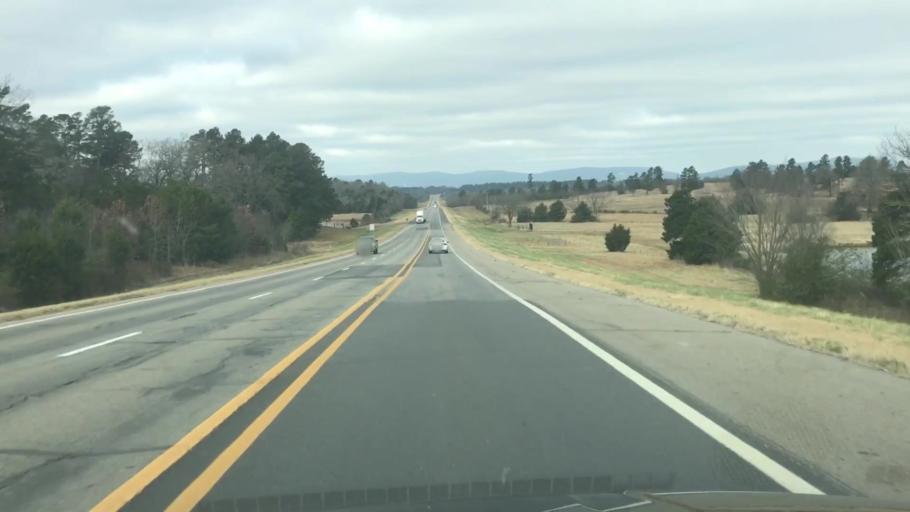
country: US
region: Arkansas
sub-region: Scott County
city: Waldron
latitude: 34.8682
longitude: -94.0790
